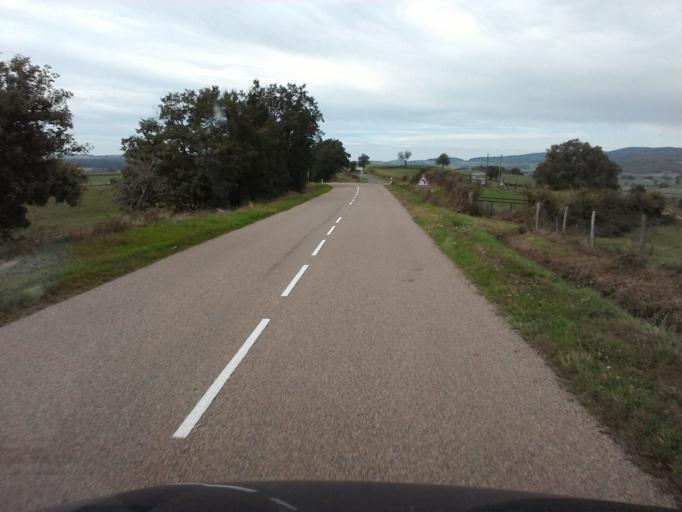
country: FR
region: Bourgogne
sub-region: Departement de Saone-et-Loire
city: Montcenis
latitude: 46.7685
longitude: 4.3661
